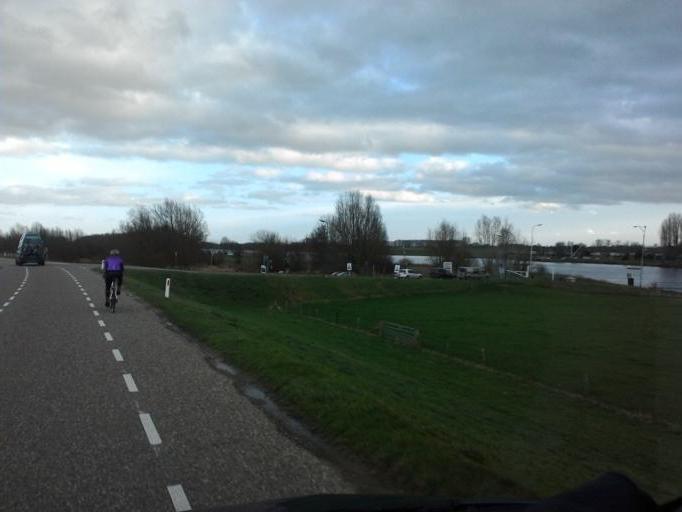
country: NL
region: Gelderland
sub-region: Gemeente Culemborg
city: Culemborg
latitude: 51.9652
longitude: 5.2804
